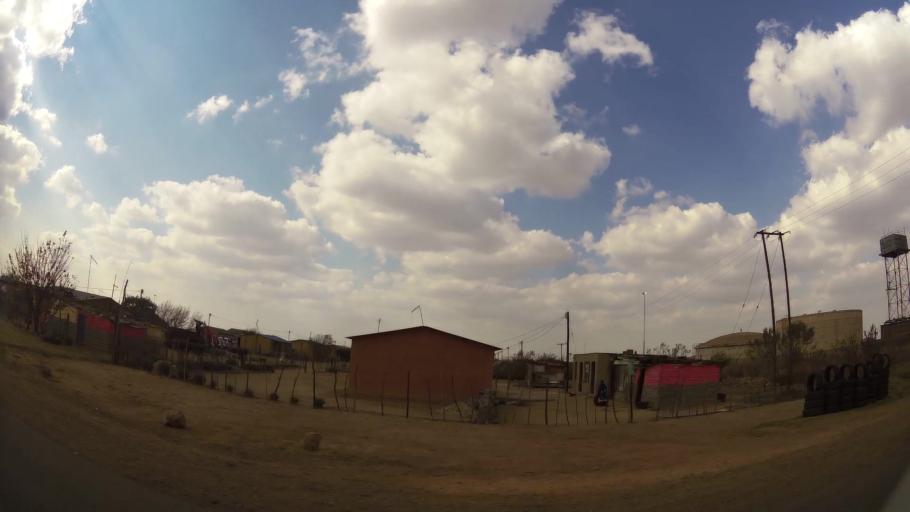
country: ZA
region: Mpumalanga
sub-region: Nkangala District Municipality
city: Delmas
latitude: -26.0977
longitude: 28.6778
